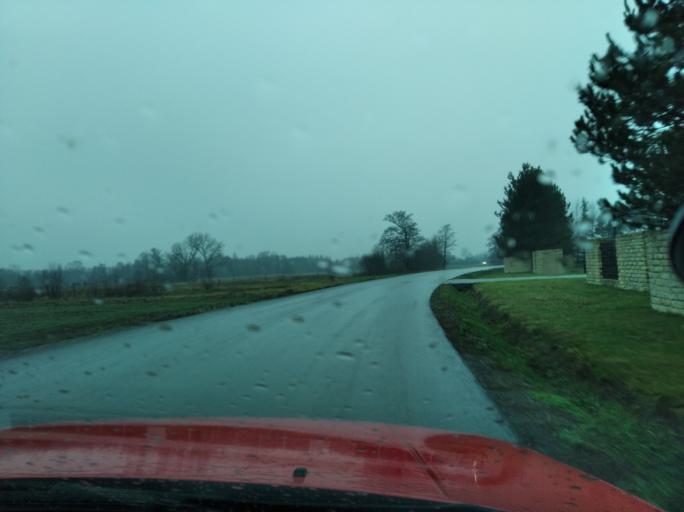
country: PL
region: Subcarpathian Voivodeship
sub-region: Powiat lancucki
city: Krzemienica
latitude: 50.0835
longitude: 22.1626
